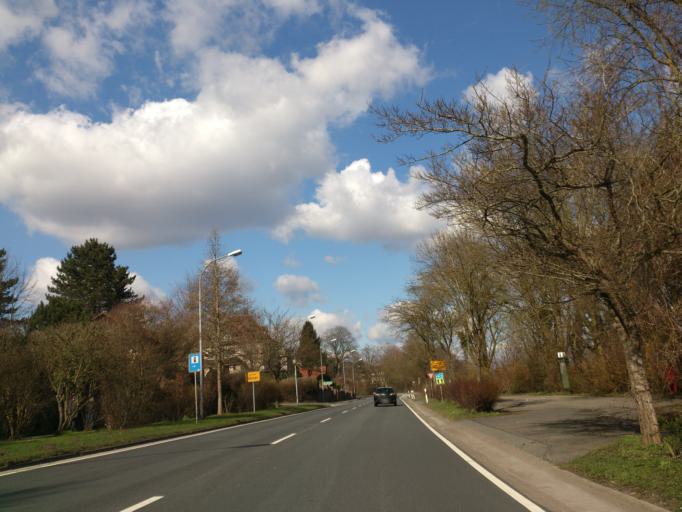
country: DE
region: North Rhine-Westphalia
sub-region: Regierungsbezirk Detmold
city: Hoexter
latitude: 51.7677
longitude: 9.3778
